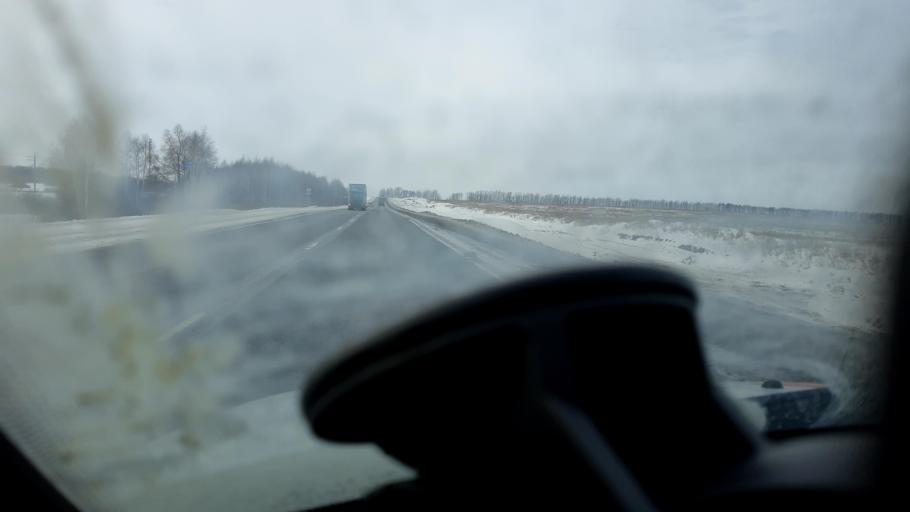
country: RU
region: Bashkortostan
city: Iglino
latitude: 54.7343
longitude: 56.2726
